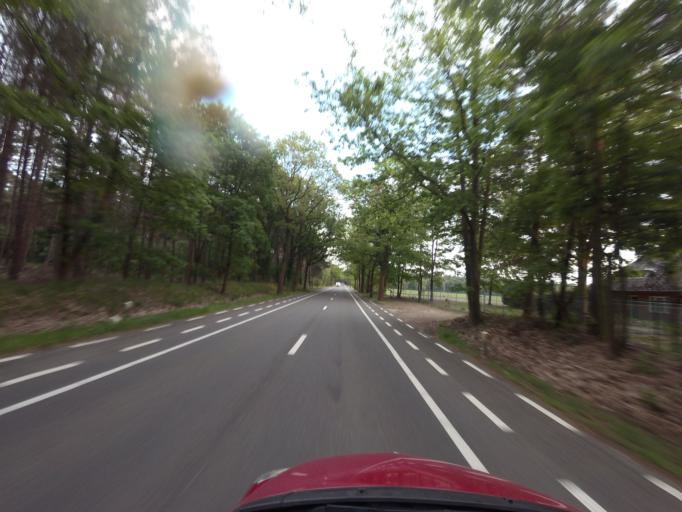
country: BE
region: Flanders
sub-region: Provincie Limburg
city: Overpelt
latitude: 51.1868
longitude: 5.3635
